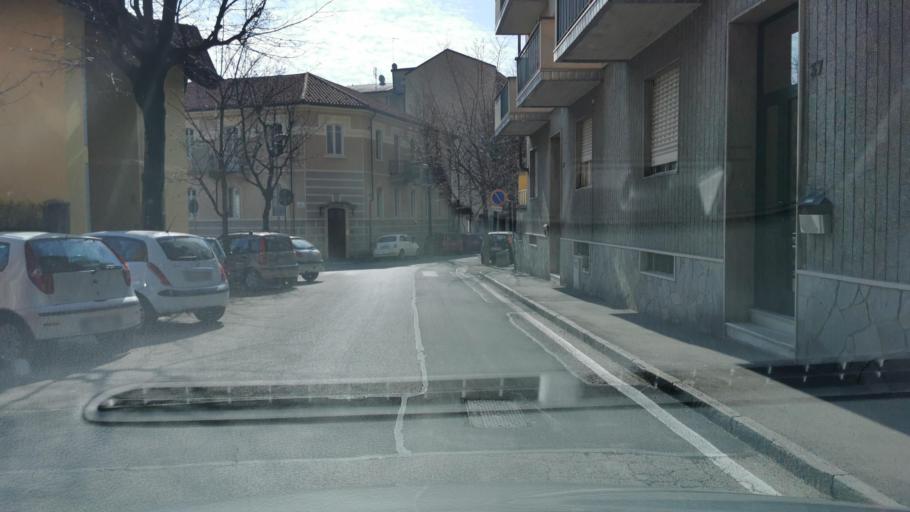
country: IT
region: Piedmont
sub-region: Provincia di Torino
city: Pinerolo
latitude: 44.8910
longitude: 7.3333
